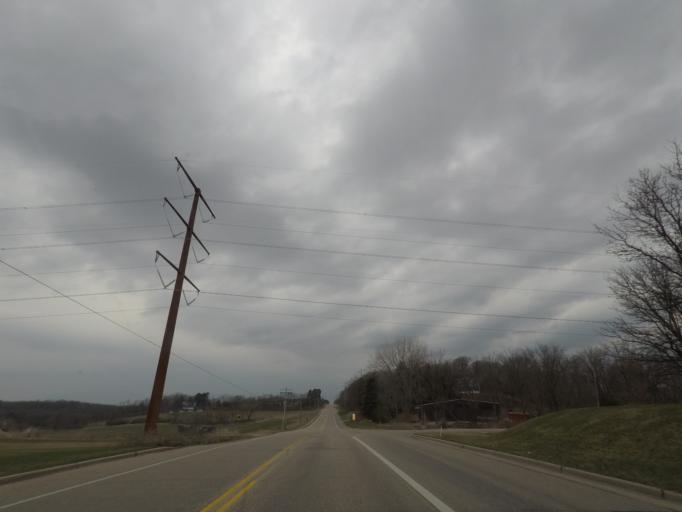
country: US
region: Wisconsin
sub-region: Dane County
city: Middleton
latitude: 43.1110
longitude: -89.5753
